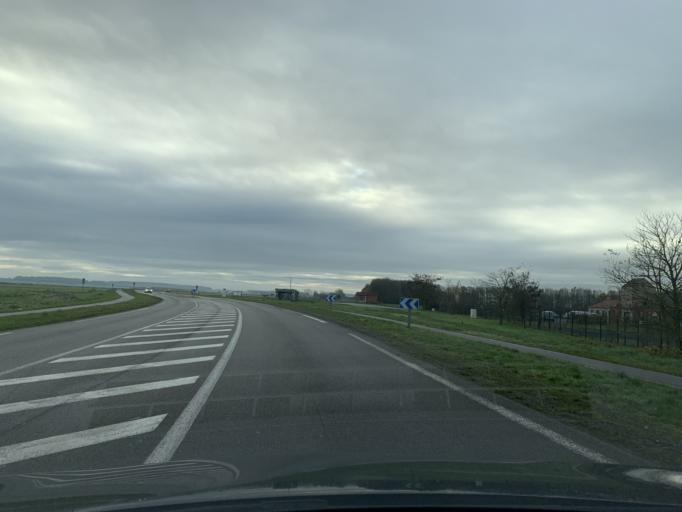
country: FR
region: Nord-Pas-de-Calais
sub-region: Departement du Nord
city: Goeulzin
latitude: 50.3308
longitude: 3.1058
